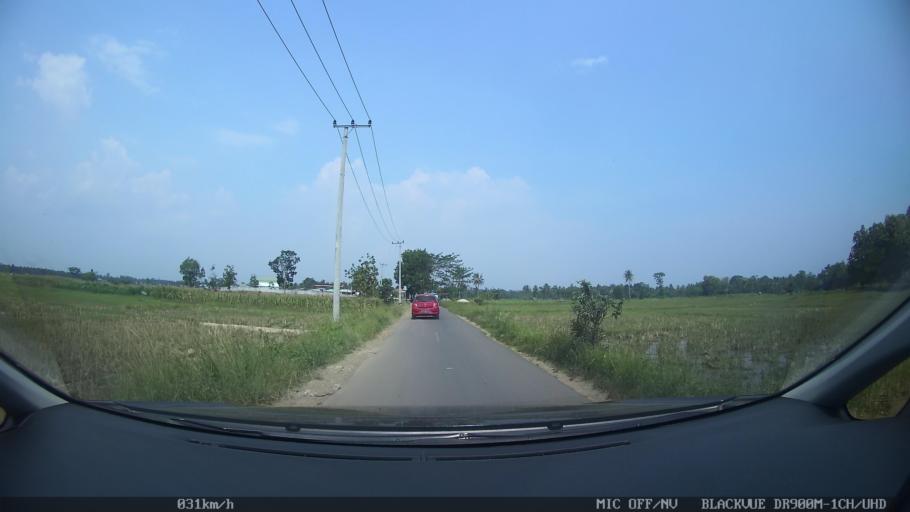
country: ID
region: Lampung
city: Natar
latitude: -5.3059
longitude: 105.2300
